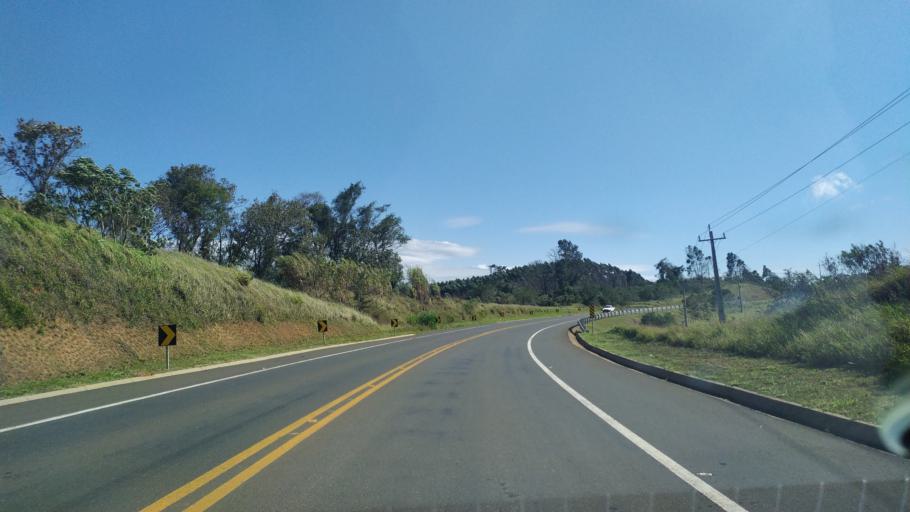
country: BR
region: Parana
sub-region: Ortigueira
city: Ortigueira
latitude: -24.2961
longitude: -50.8221
